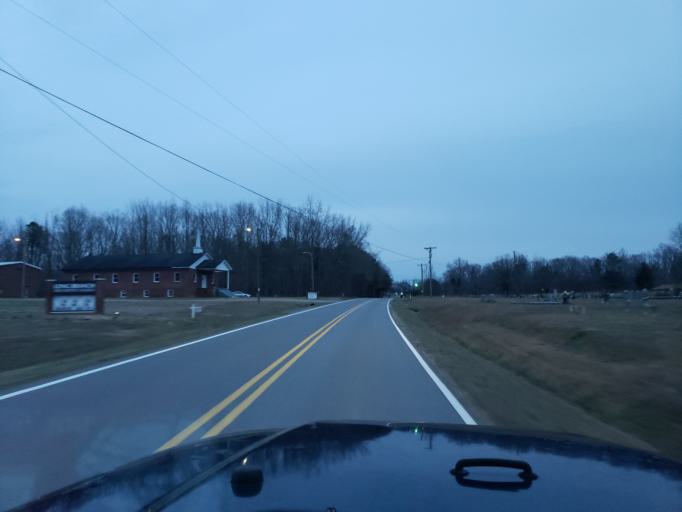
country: US
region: North Carolina
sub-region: Cleveland County
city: White Plains
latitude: 35.2022
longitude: -81.4494
